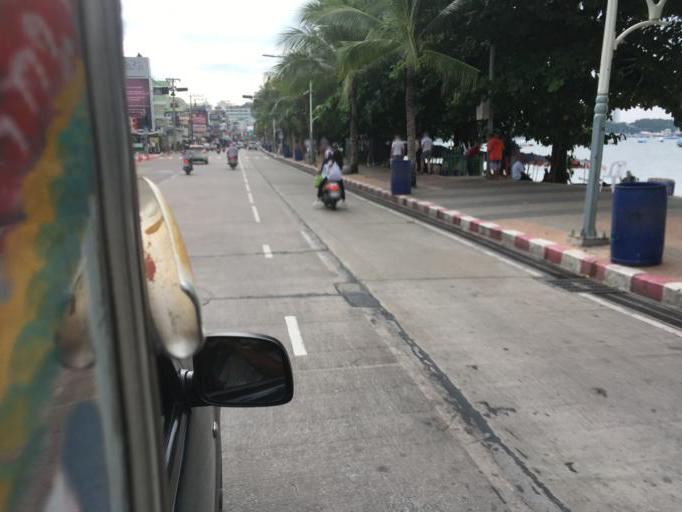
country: TH
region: Chon Buri
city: Phatthaya
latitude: 12.9302
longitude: 100.8779
